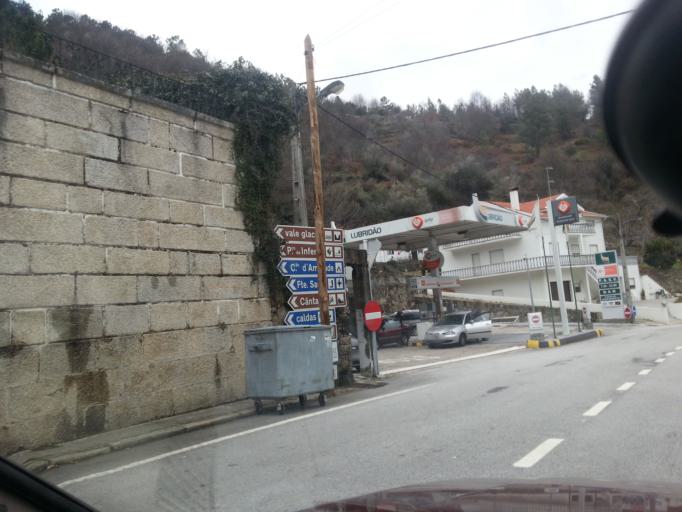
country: PT
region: Guarda
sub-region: Manteigas
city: Manteigas
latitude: 40.3941
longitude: -7.5434
